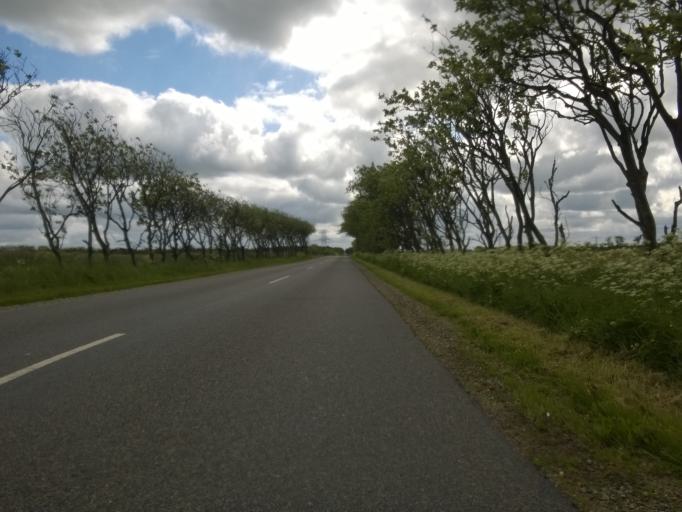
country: DK
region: Central Jutland
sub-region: Holstebro Kommune
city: Vinderup
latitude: 56.4123
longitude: 8.8369
